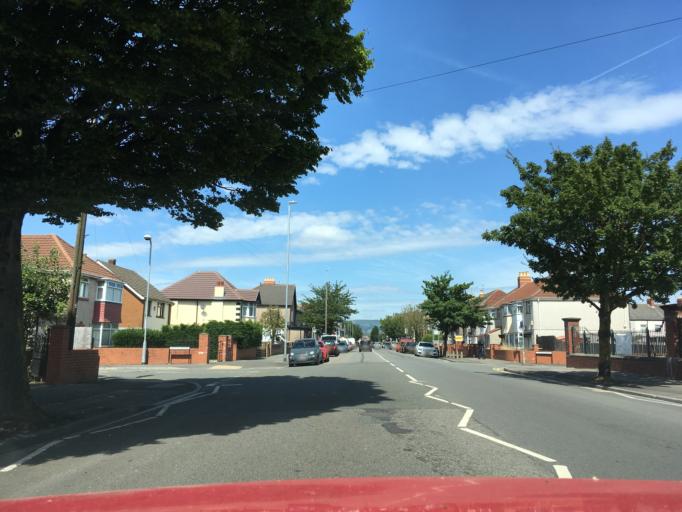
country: GB
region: Wales
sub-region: Newport
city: Newport
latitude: 51.5809
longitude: -2.9716
